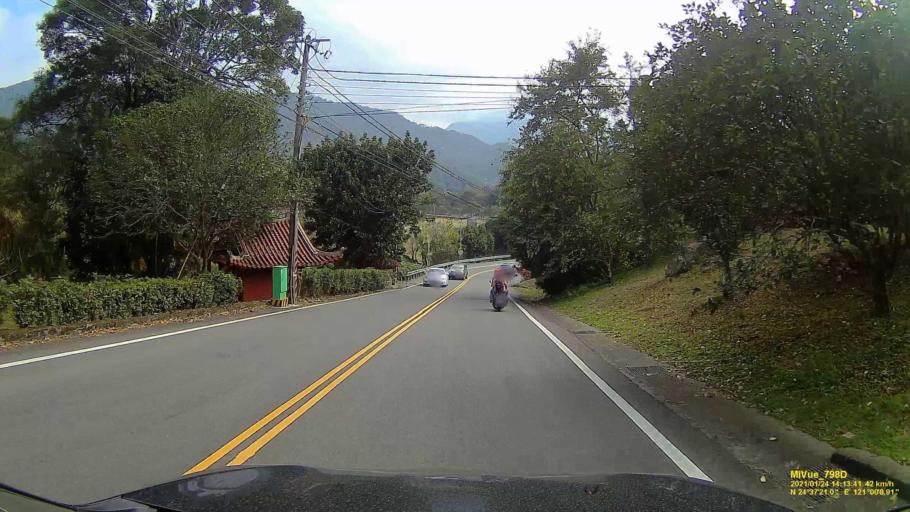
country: TW
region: Taiwan
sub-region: Hsinchu
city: Hsinchu
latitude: 24.6221
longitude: 121.0025
